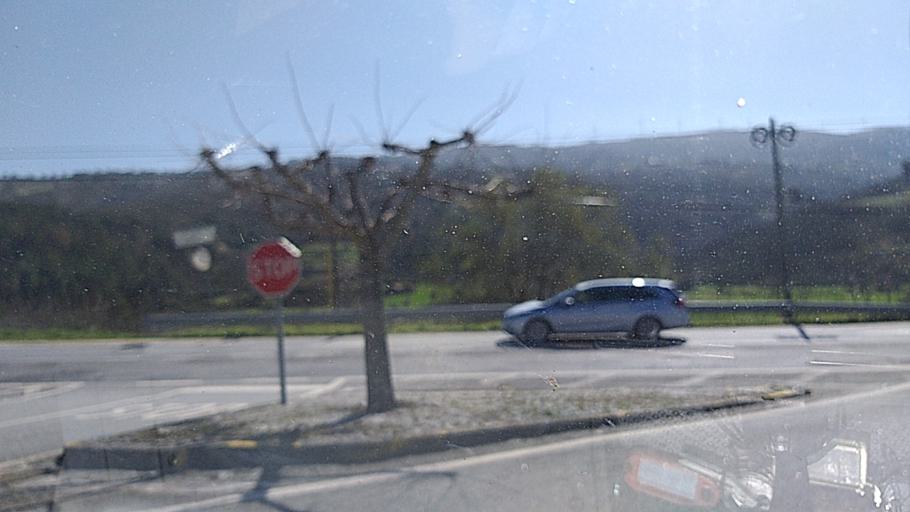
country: PT
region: Guarda
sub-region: Celorico da Beira
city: Celorico da Beira
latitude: 40.6162
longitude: -7.4069
